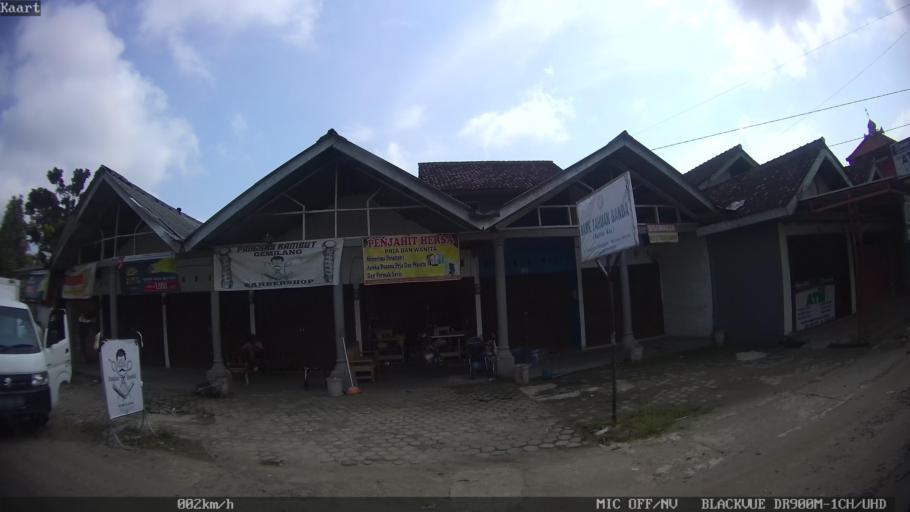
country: ID
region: Lampung
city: Kedaton
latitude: -5.3202
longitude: 105.2864
